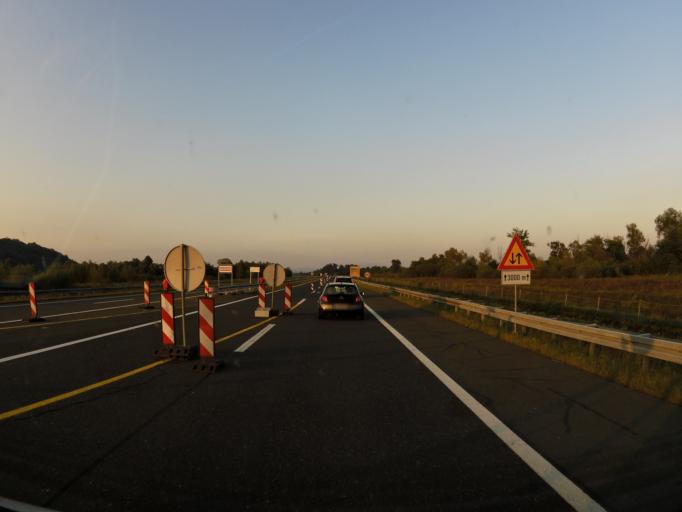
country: HR
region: Zagrebacka
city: Jakovlje
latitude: 45.9604
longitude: 15.8432
